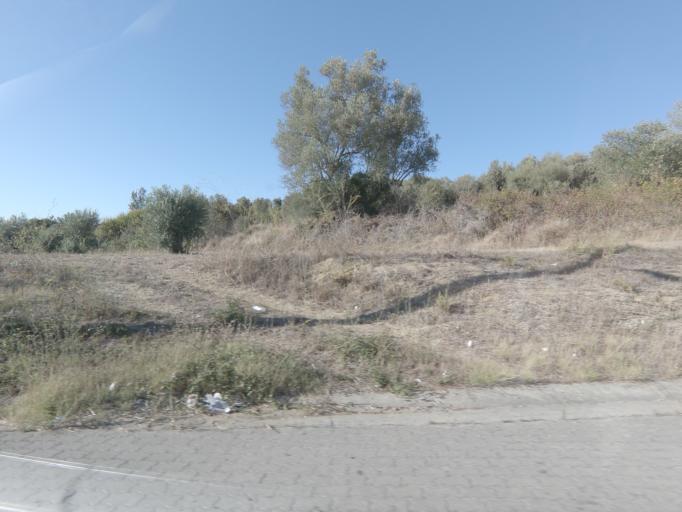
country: PT
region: Setubal
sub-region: Palmela
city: Quinta do Anjo
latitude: 38.5667
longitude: -8.9264
